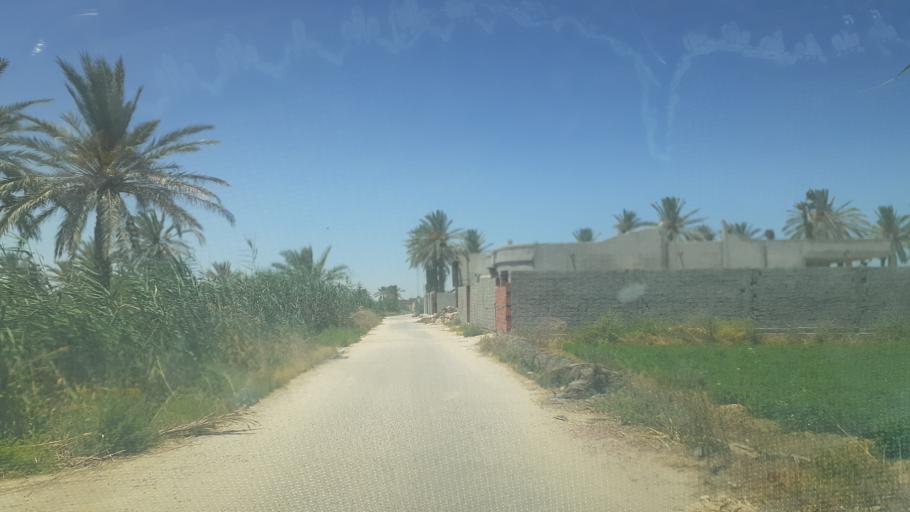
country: TN
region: Qabis
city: Gabes
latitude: 33.9280
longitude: 10.0606
